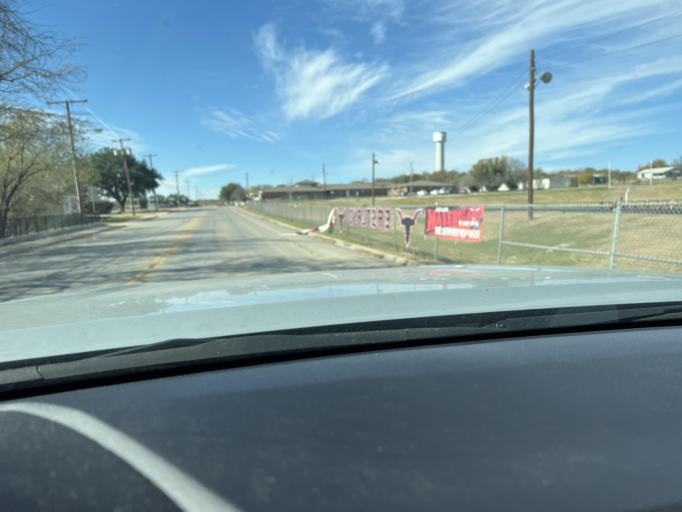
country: US
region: Texas
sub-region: Eastland County
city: Eastland
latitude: 32.3955
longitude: -98.8279
